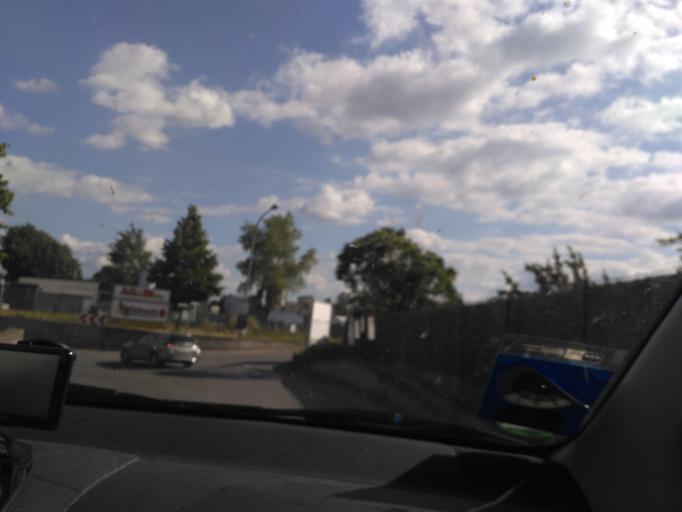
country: DE
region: Saxony
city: Weinbohla
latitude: 51.1624
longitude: 13.5598
